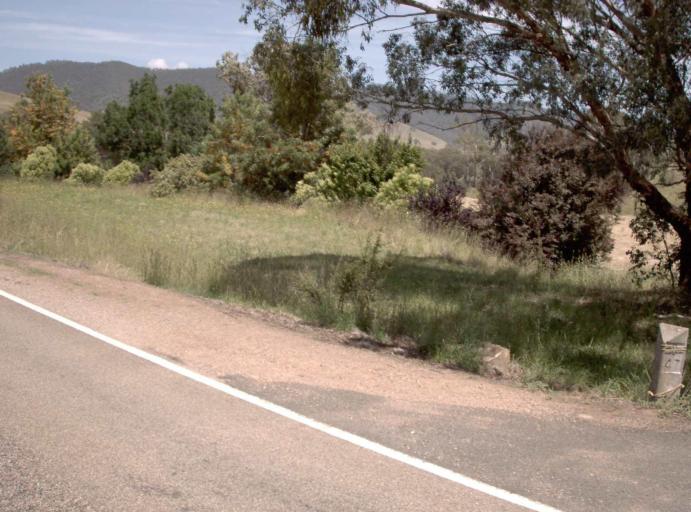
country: AU
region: Victoria
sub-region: East Gippsland
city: Bairnsdale
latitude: -37.3794
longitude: 147.8306
